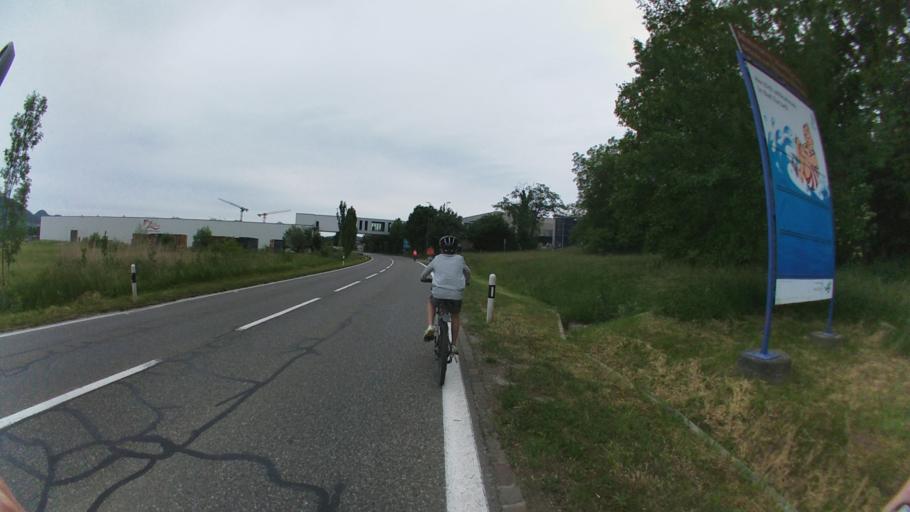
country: CH
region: Aargau
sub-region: Bezirk Zurzach
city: Bad Zurzach
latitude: 47.5971
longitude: 8.2843
